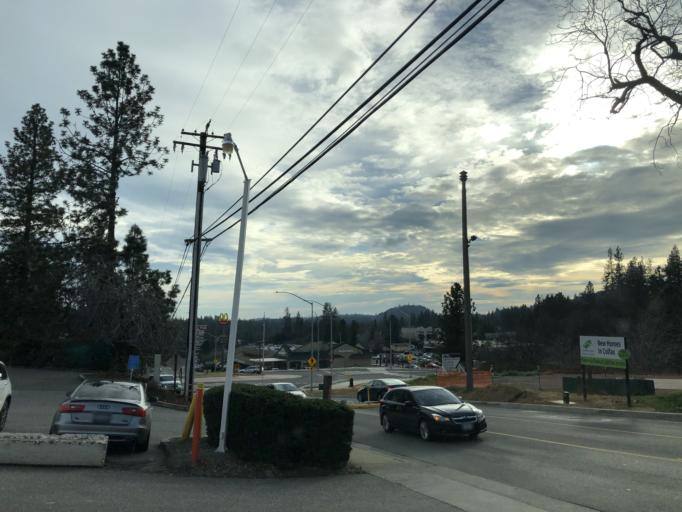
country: US
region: California
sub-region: Placer County
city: Colfax
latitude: 39.0955
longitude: -120.9507
